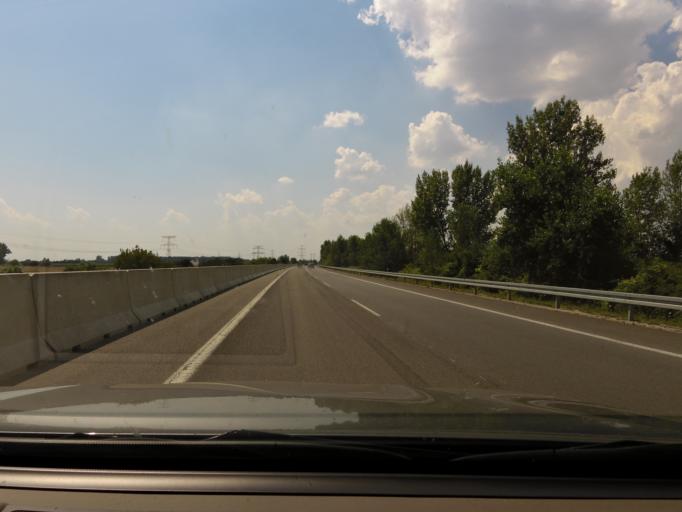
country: SK
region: Trnavsky
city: Leopoldov
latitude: 48.3694
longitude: 17.7157
